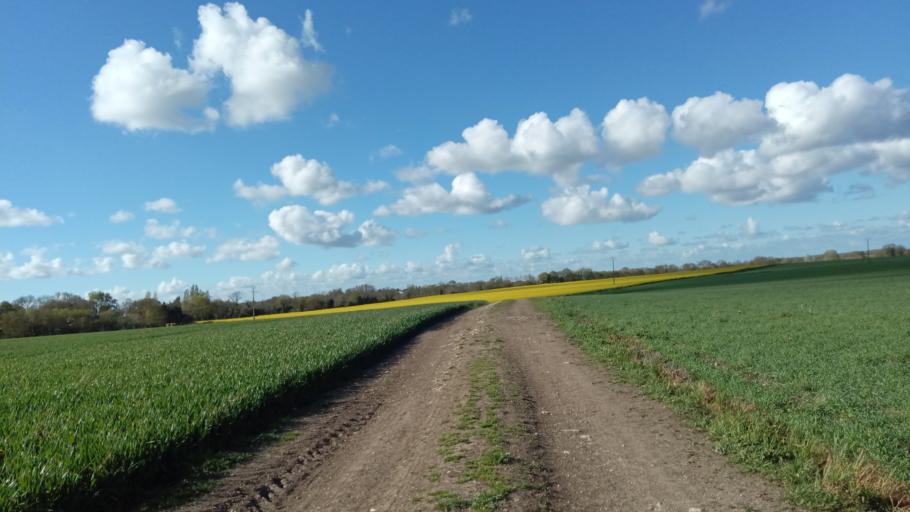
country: FR
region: Poitou-Charentes
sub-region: Departement de la Charente-Maritime
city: Verines
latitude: 46.1656
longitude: -0.9406
